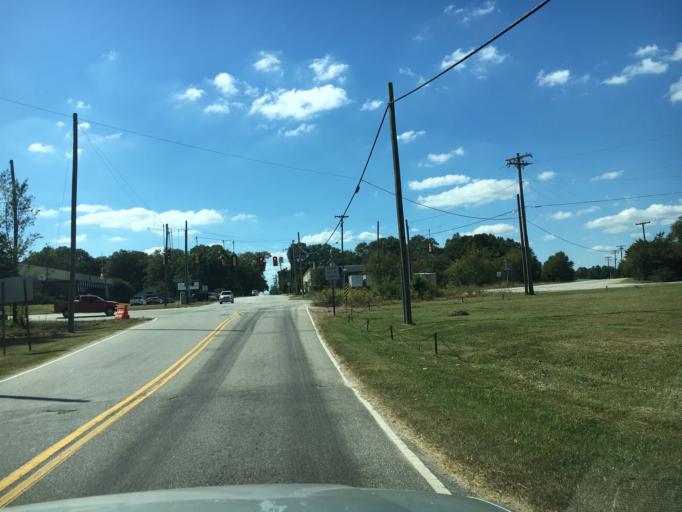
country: US
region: South Carolina
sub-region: Greenville County
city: Greenville
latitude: 34.8443
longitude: -82.3543
